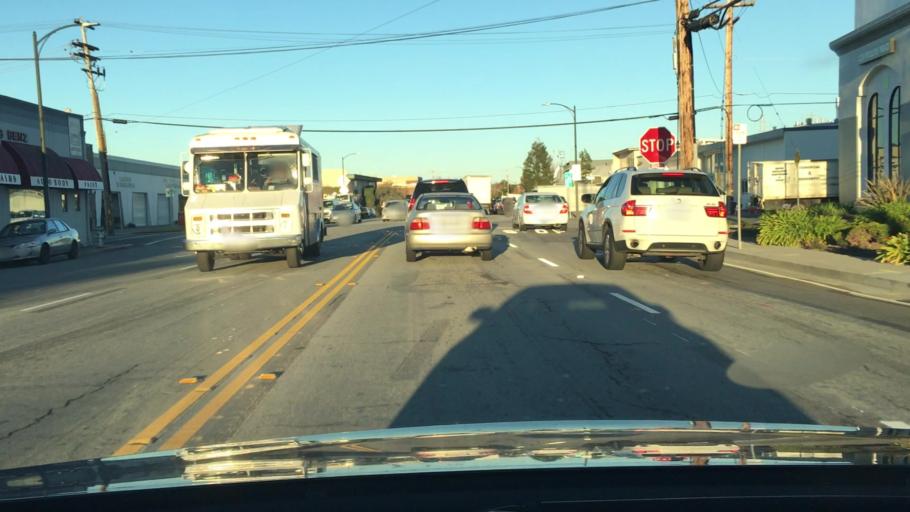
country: US
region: California
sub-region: San Mateo County
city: Burlingame
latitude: 37.5897
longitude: -122.3639
